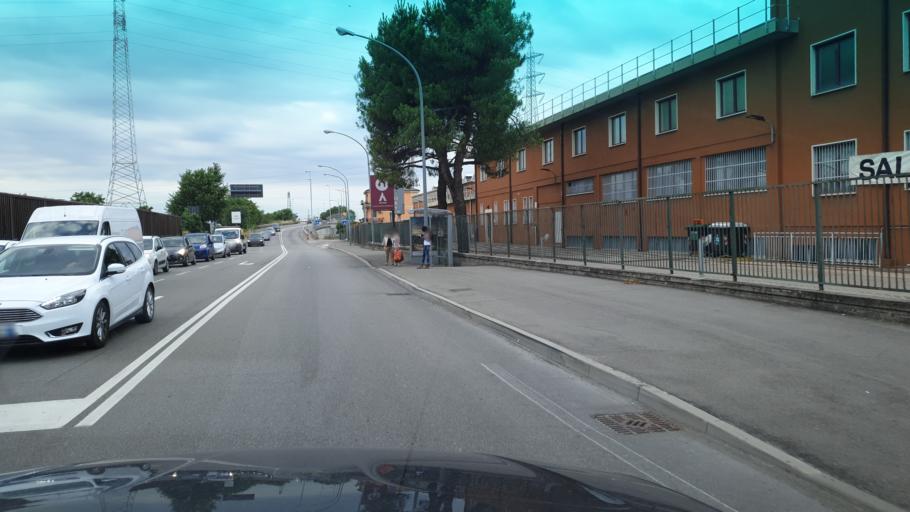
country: IT
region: Veneto
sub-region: Provincia di Verona
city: Verona
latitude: 45.3996
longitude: 10.9809
